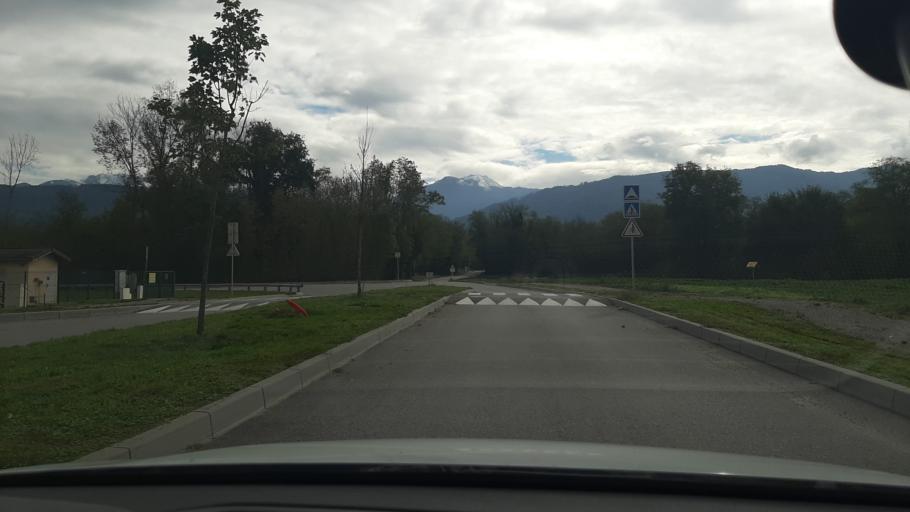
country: FR
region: Rhone-Alpes
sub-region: Departement de la Savoie
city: Montmelian
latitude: 45.4744
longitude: 6.0346
